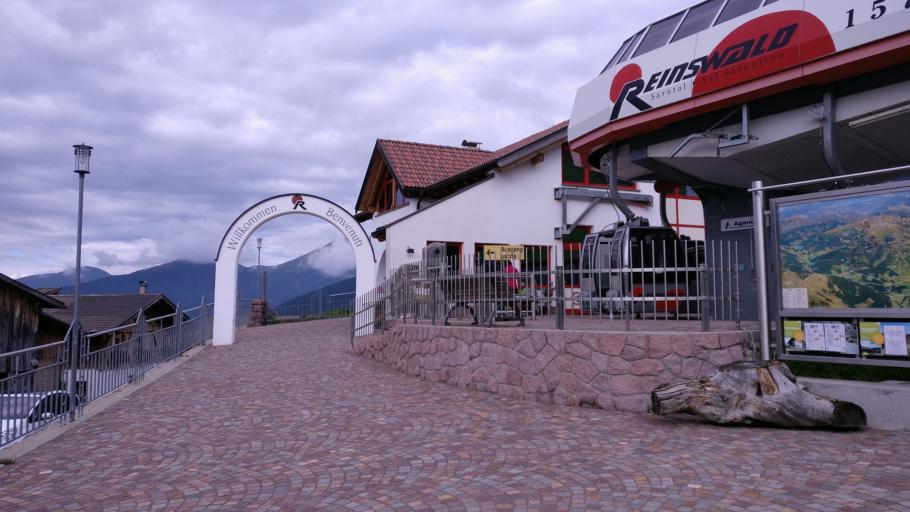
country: IT
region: Trentino-Alto Adige
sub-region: Bolzano
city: Sarentino
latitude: 46.6881
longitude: 11.4208
